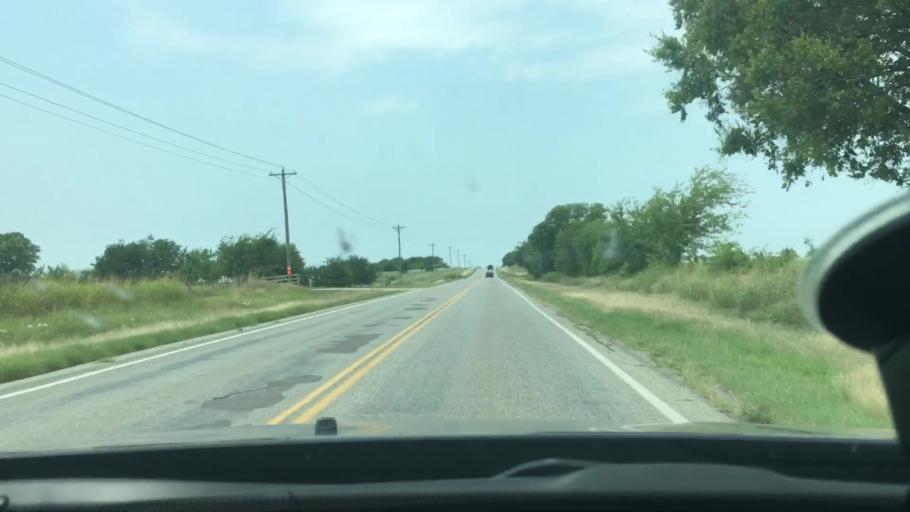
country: US
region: Oklahoma
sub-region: Marshall County
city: Kingston
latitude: 33.9983
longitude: -96.7680
